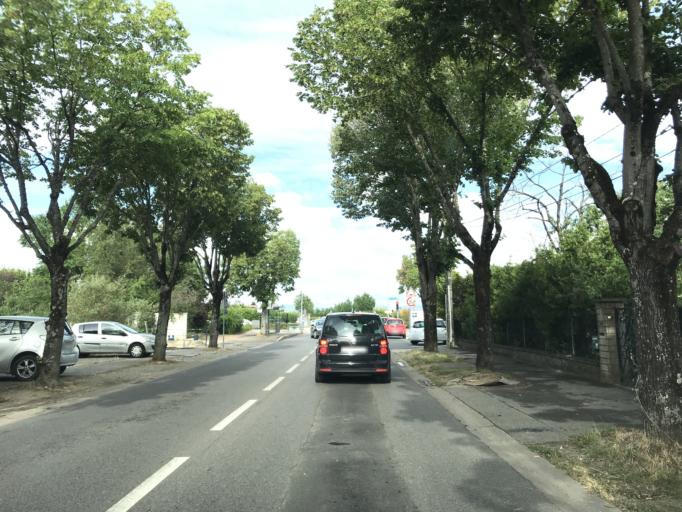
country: FR
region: Rhone-Alpes
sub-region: Departement du Rhone
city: Mions
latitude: 45.6693
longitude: 4.9516
